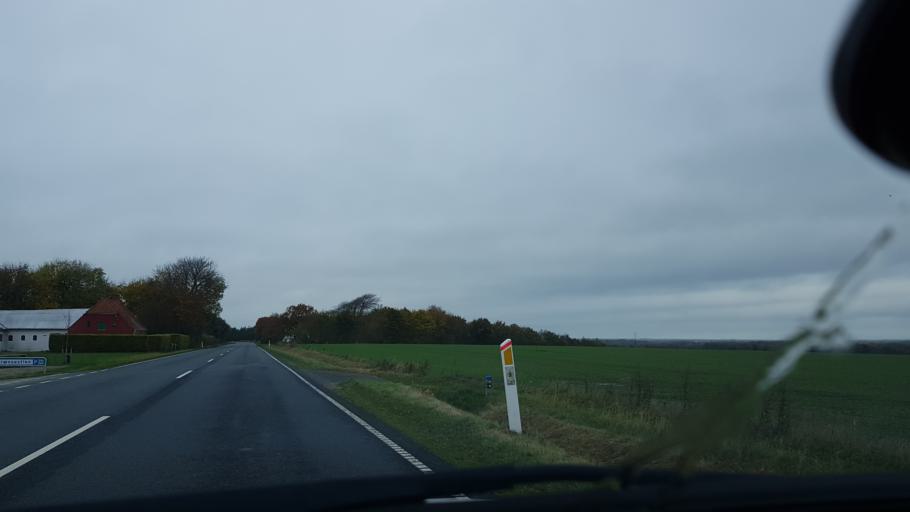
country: DK
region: South Denmark
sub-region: Esbjerg Kommune
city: Ribe
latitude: 55.2763
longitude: 8.8629
